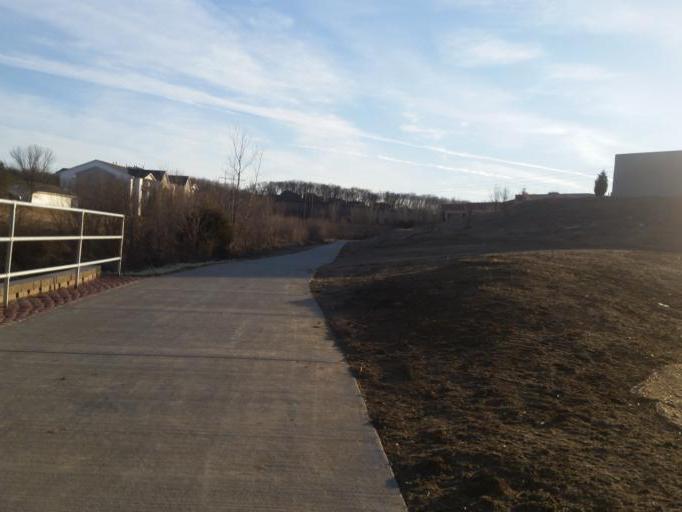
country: US
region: Nebraska
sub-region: Sarpy County
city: Offutt Air Force Base
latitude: 41.1396
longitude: -95.9734
